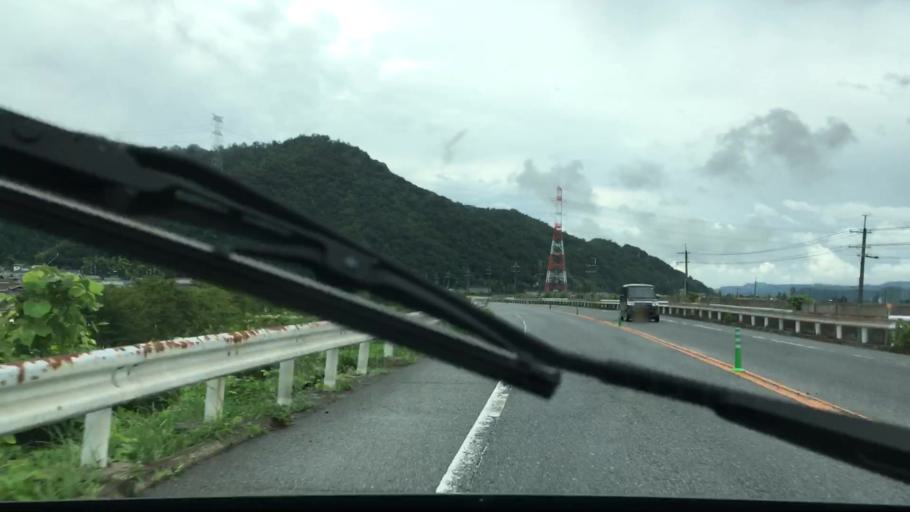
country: JP
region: Hyogo
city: Himeji
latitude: 34.9773
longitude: 134.7687
